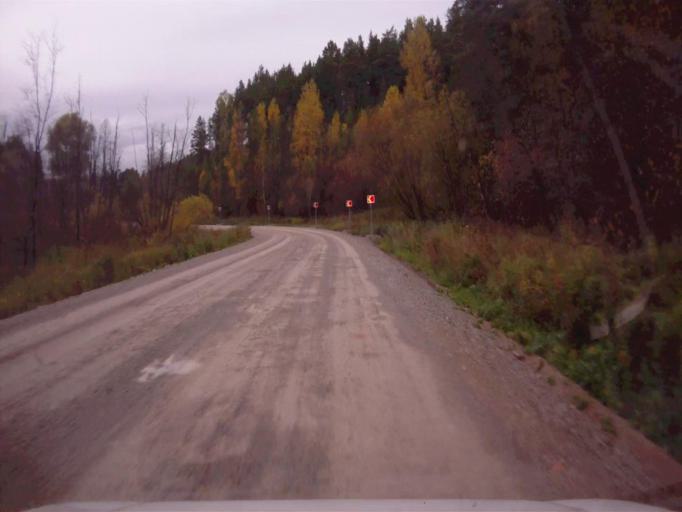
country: RU
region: Chelyabinsk
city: Nyazepetrovsk
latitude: 56.0465
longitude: 59.5030
